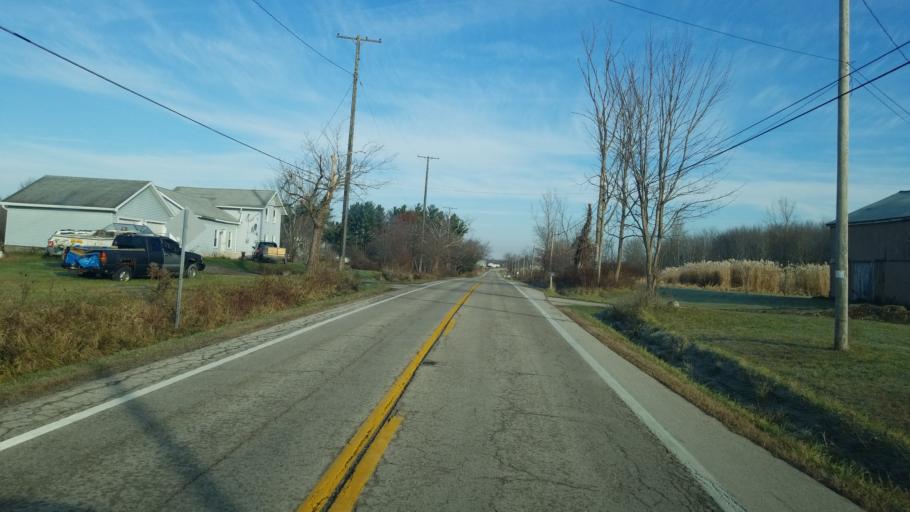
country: US
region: Ohio
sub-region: Ashtabula County
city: North Kingsville
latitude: 41.8012
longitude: -80.6691
